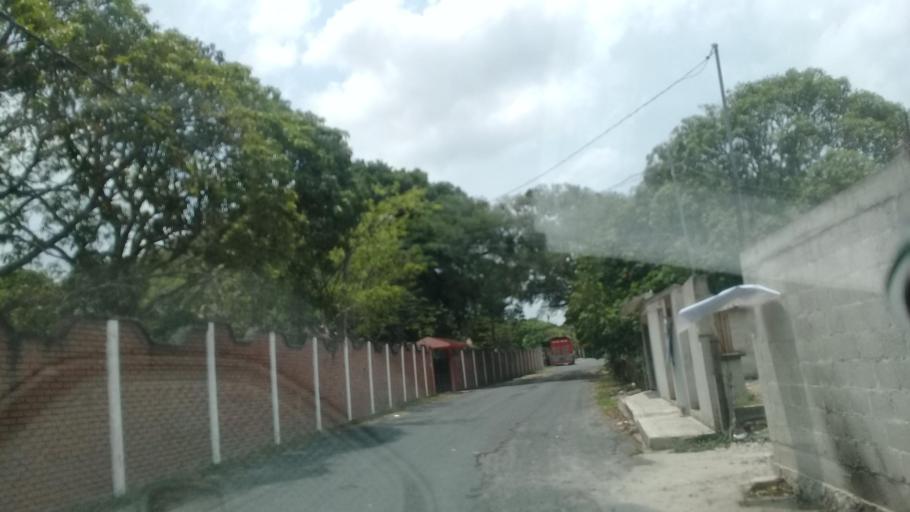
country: MX
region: Veracruz
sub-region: Emiliano Zapata
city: Plan del Rio
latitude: 19.4292
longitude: -96.6972
